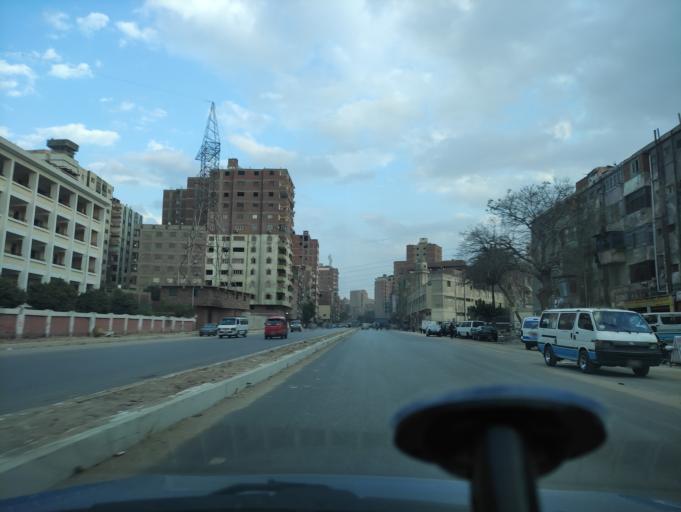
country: EG
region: Muhafazat al Qalyubiyah
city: Al Khankah
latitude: 30.1337
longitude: 31.3575
